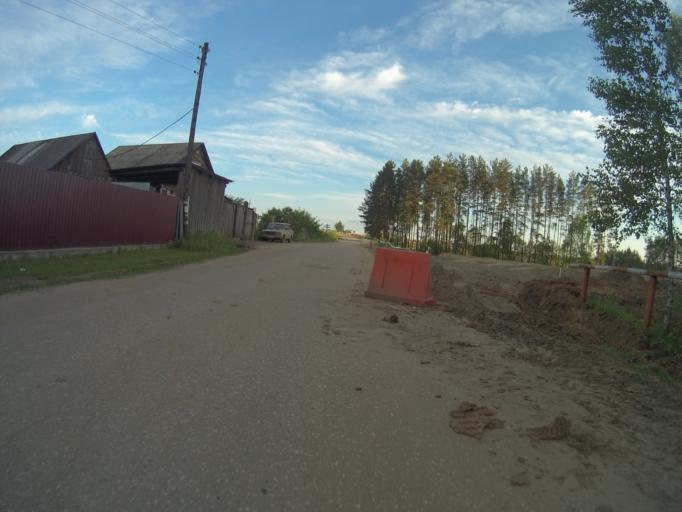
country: RU
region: Vladimir
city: Kommunar
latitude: 56.0740
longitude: 40.4908
